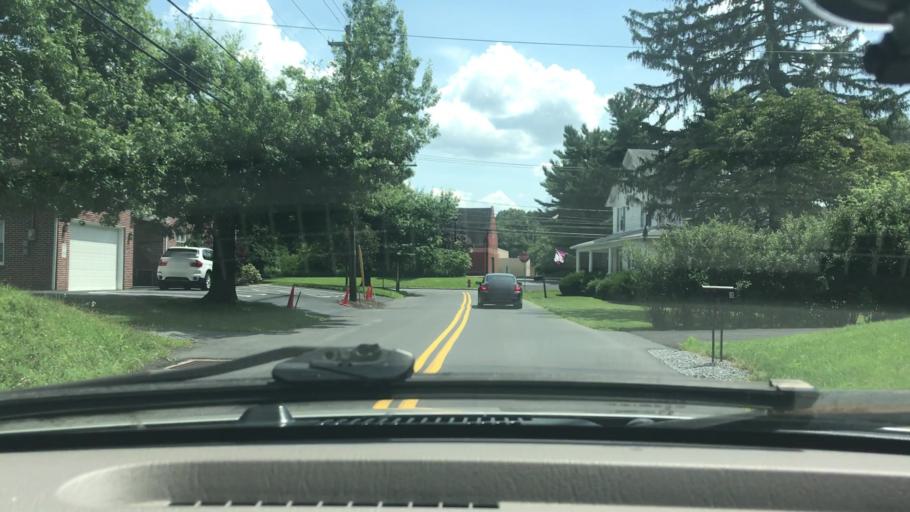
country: US
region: Pennsylvania
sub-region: Dauphin County
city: Paxtonia
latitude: 40.3194
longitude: -76.7908
